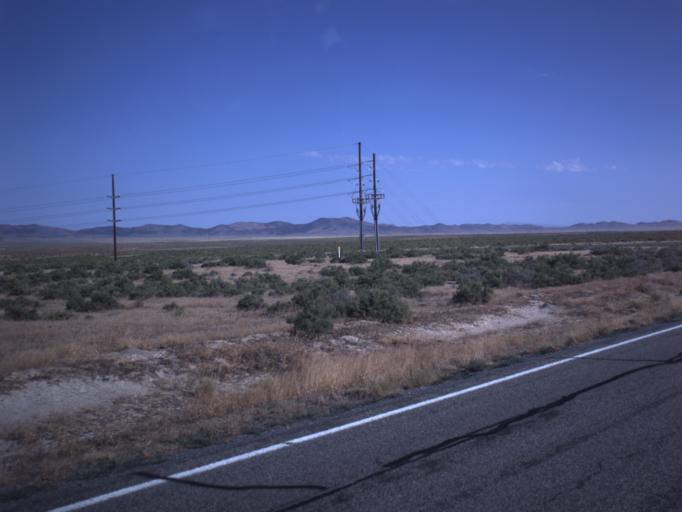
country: US
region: Utah
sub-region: Beaver County
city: Milford
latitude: 38.5004
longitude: -112.9911
